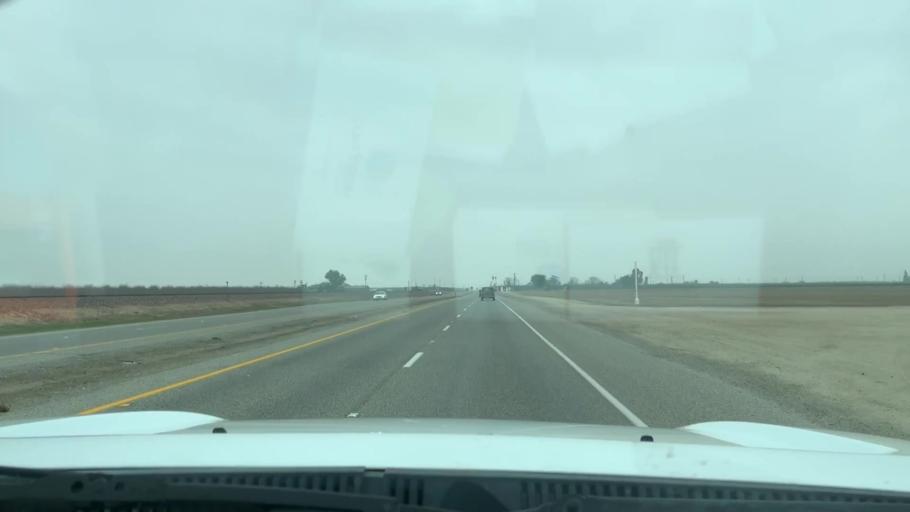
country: US
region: California
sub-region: Kern County
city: Shafter
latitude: 35.5240
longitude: -119.3001
